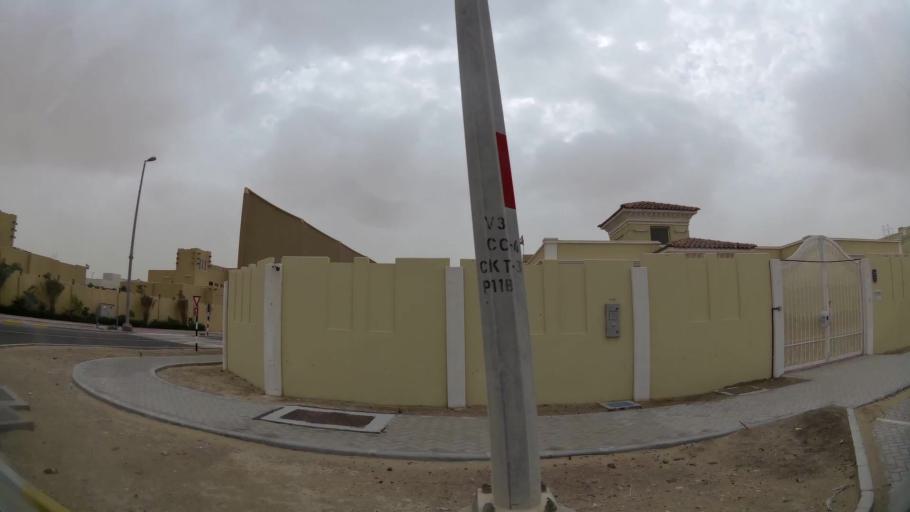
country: AE
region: Abu Dhabi
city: Abu Dhabi
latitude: 24.4484
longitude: 54.7317
